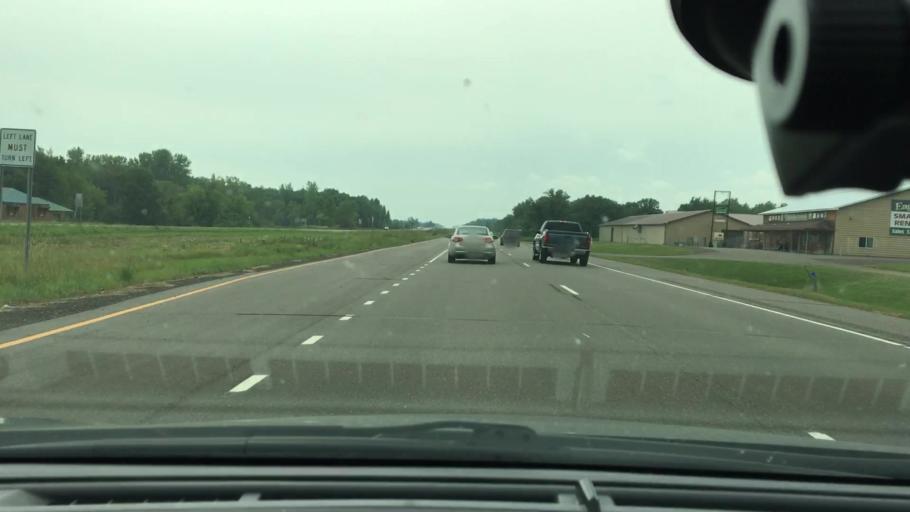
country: US
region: Minnesota
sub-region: Mille Lacs County
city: Vineland
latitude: 46.0530
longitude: -93.6629
